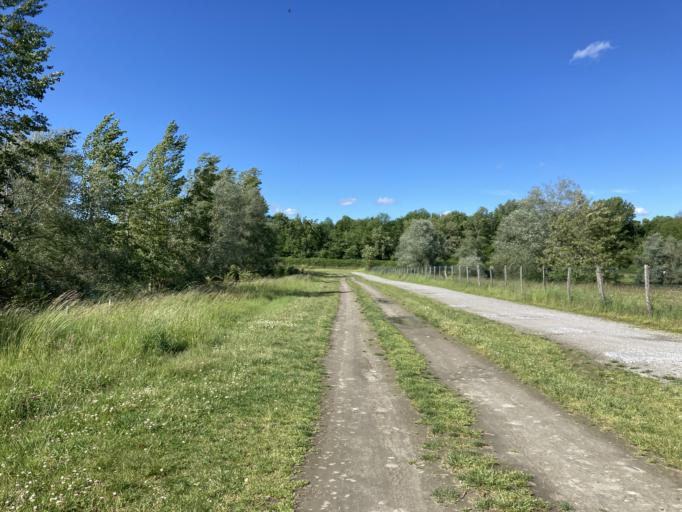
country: FR
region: Aquitaine
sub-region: Departement des Pyrenees-Atlantiques
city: Artiguelouve
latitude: 43.3086
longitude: -0.4389
